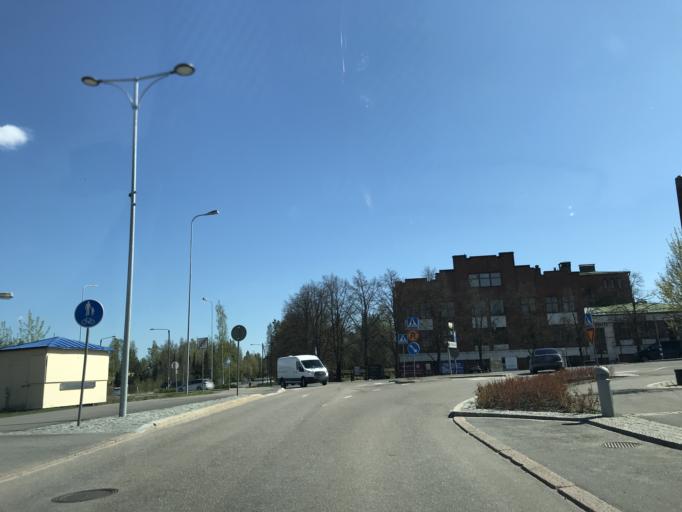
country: FI
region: Paijanne Tavastia
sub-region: Lahti
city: Orimattila
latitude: 60.8024
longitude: 25.7347
